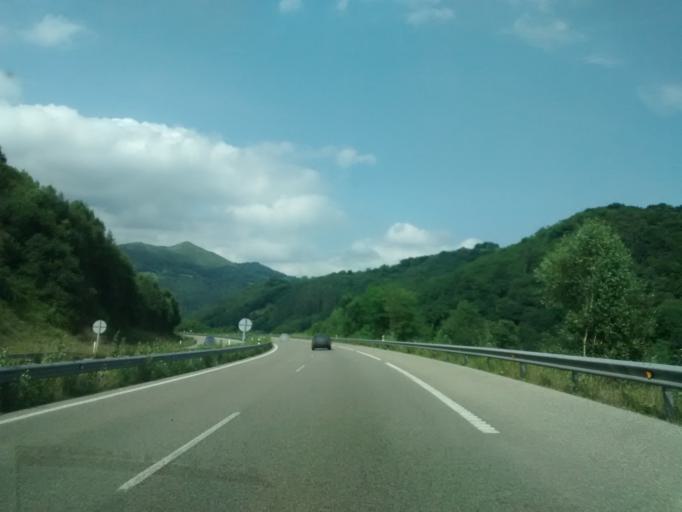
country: ES
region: Asturias
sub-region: Province of Asturias
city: Mieres
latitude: 43.3074
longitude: -5.7474
